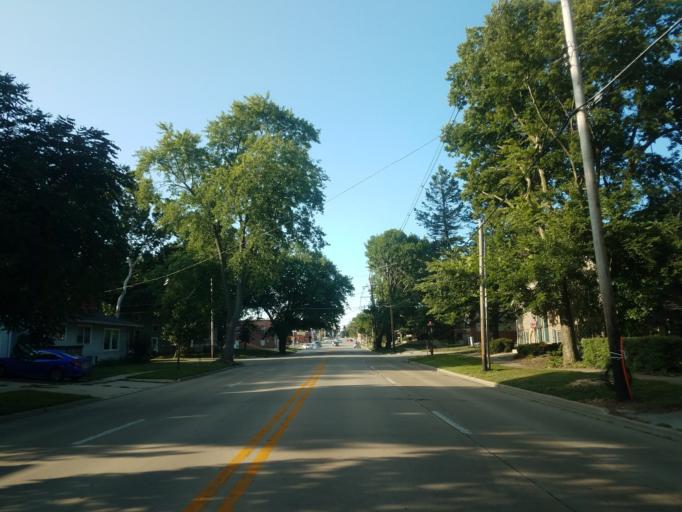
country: US
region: Illinois
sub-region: McLean County
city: Normal
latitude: 40.5128
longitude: -88.9825
